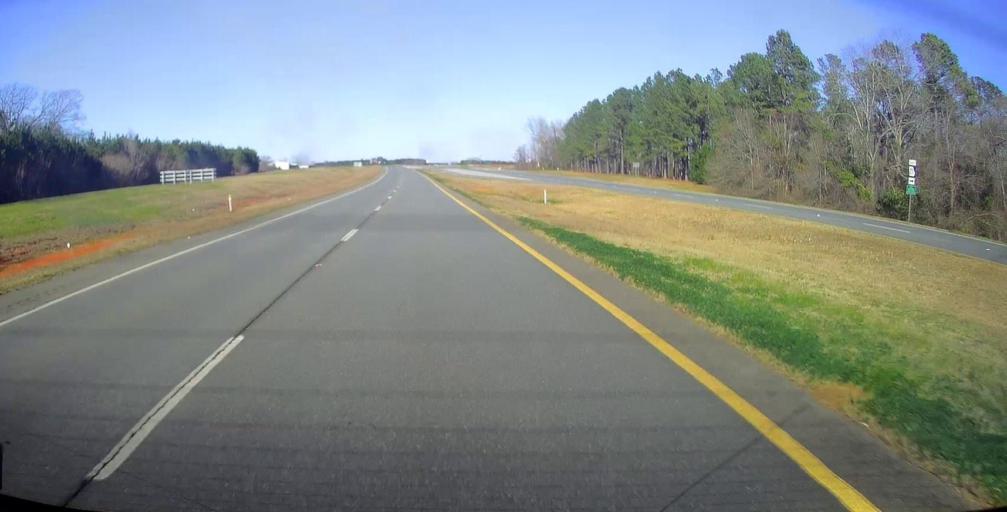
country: US
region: Georgia
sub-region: Schley County
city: Ellaville
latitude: 32.1806
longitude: -84.2679
